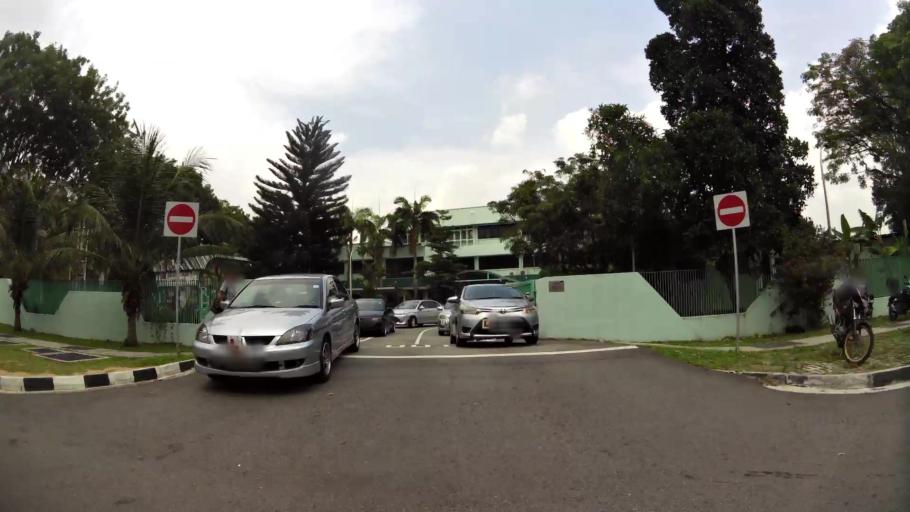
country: SG
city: Singapore
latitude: 1.3353
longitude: 103.8968
